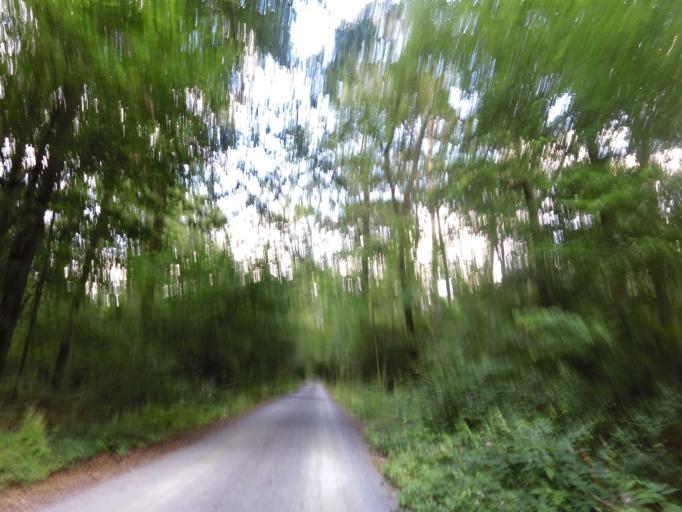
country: DE
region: Hesse
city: Niederrad
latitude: 50.0543
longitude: 8.6199
